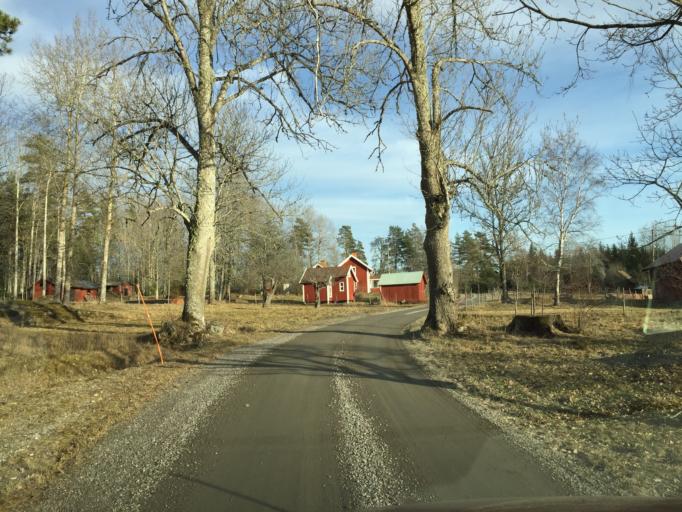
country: SE
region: OErebro
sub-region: Orebro Kommun
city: Odensbacken
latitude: 59.1014
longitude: 15.5496
